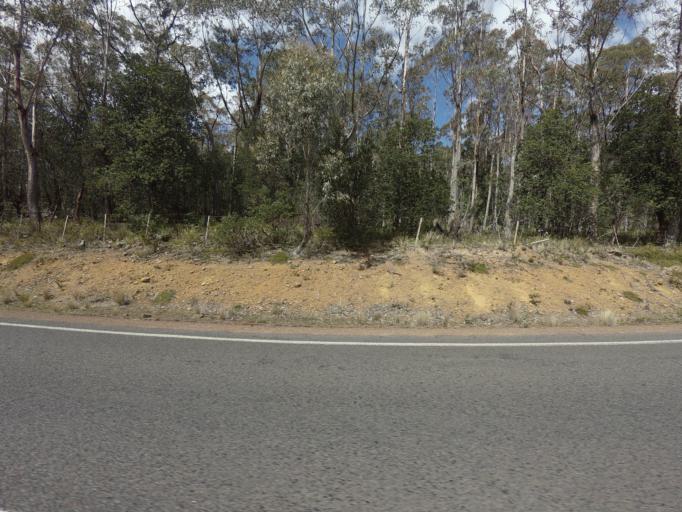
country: AU
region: Tasmania
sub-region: Northern Midlands
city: Evandale
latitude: -42.0049
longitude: 147.7230
